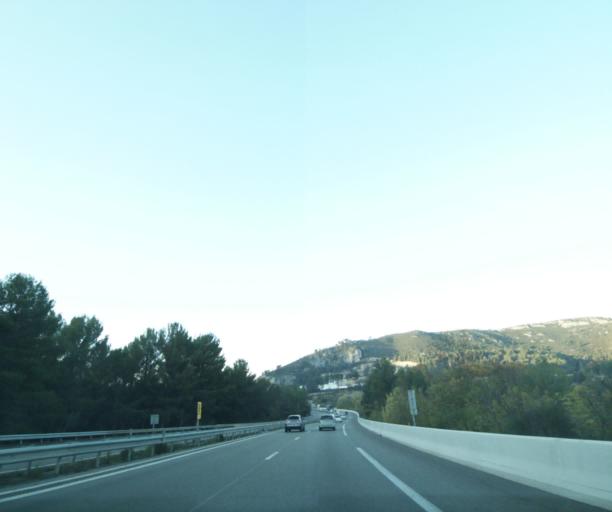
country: FR
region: Provence-Alpes-Cote d'Azur
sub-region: Departement des Bouches-du-Rhone
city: Roquevaire
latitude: 43.3620
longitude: 5.6142
